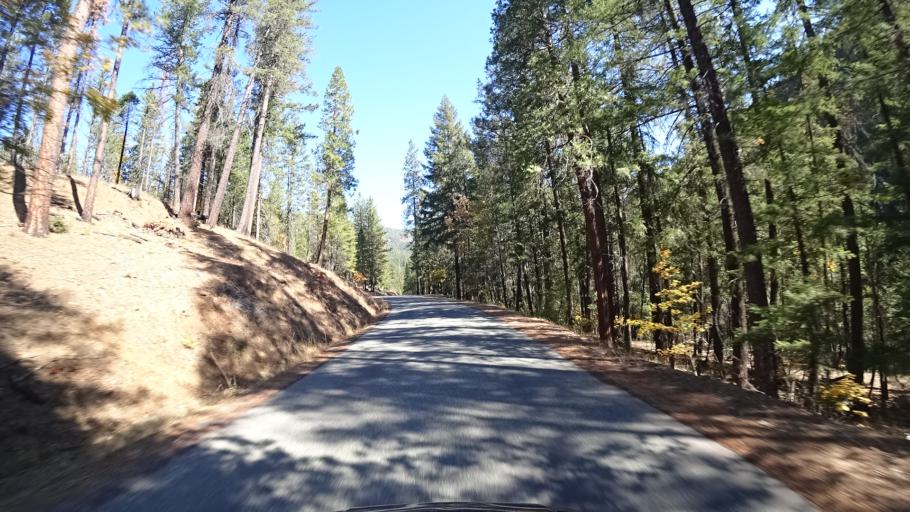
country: US
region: California
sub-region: Siskiyou County
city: Happy Camp
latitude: 41.6393
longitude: -123.0538
